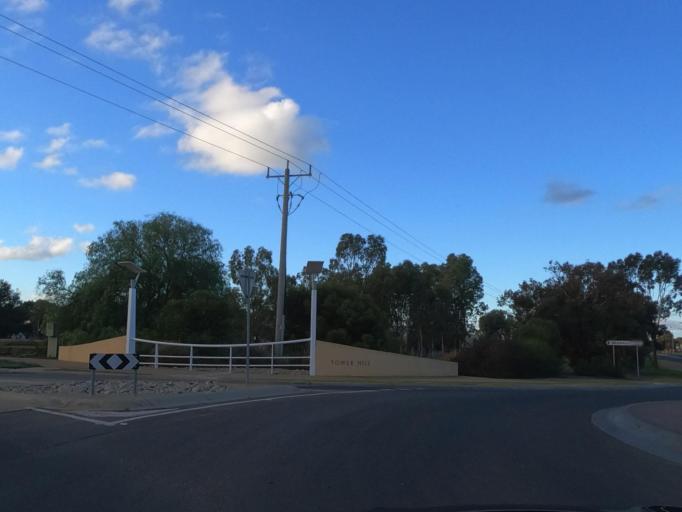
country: AU
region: Victoria
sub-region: Swan Hill
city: Swan Hill
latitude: -35.3430
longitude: 143.5314
